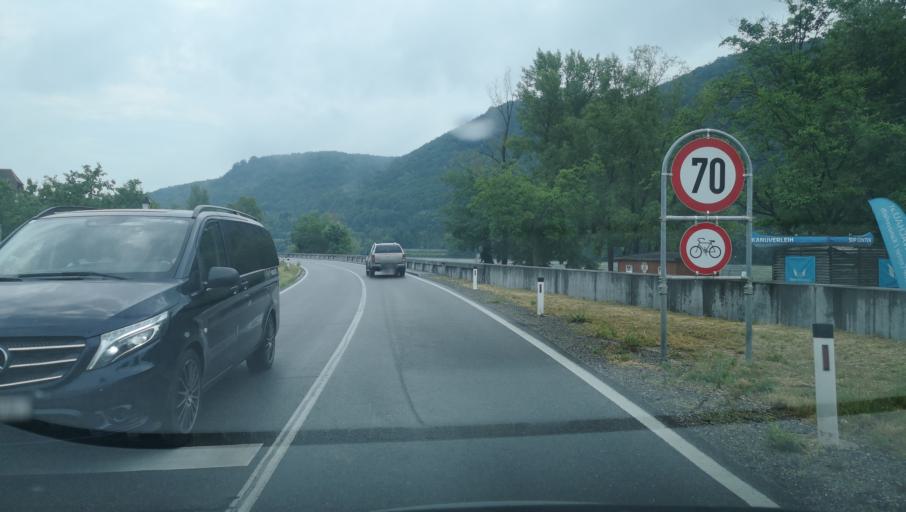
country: AT
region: Lower Austria
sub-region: Politischer Bezirk Krems
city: Durnstein
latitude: 48.3858
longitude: 15.5330
